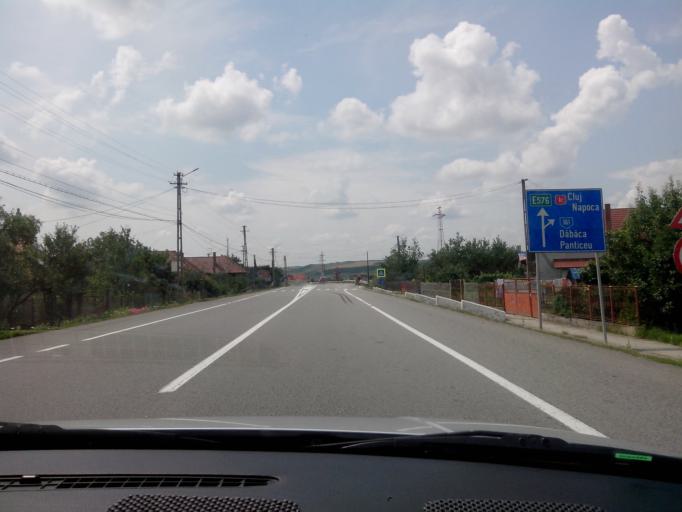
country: RO
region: Cluj
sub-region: Comuna Iclod
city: Iclod
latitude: 46.9427
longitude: 23.7911
